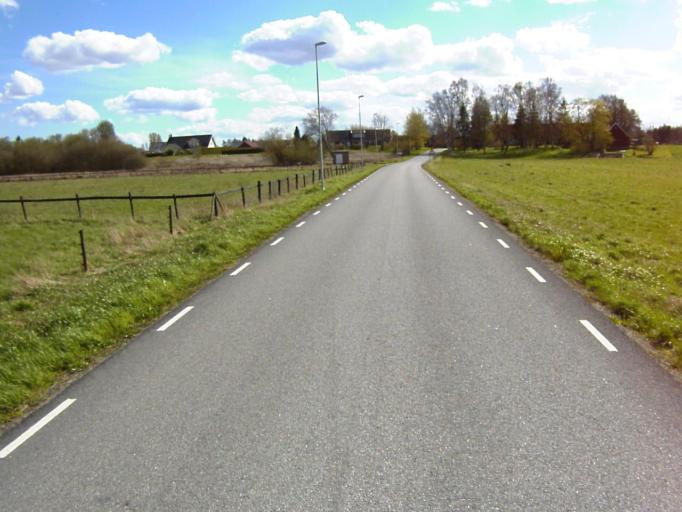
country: SE
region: Skane
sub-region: Kristianstads Kommun
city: Kristianstad
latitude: 56.0134
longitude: 14.0908
